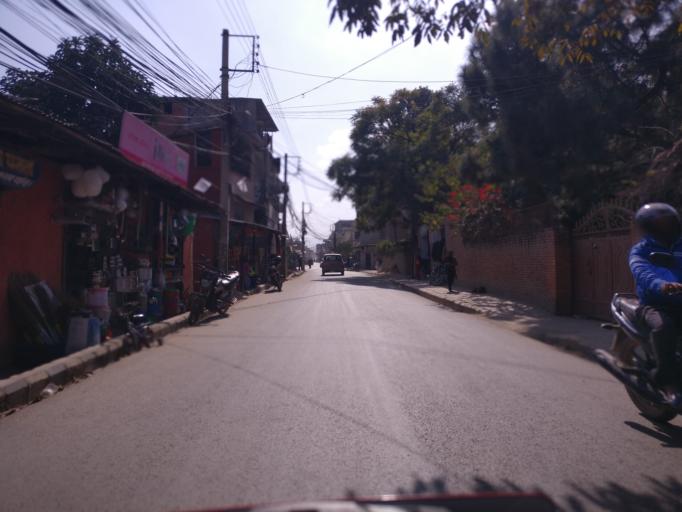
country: NP
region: Central Region
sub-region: Bagmati Zone
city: Patan
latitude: 27.6685
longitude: 85.3131
